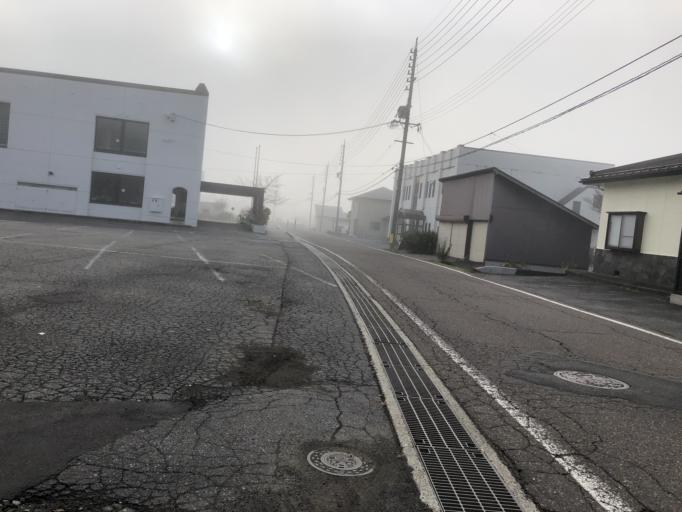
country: JP
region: Nagano
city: Nagano-shi
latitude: 36.8061
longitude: 138.2011
